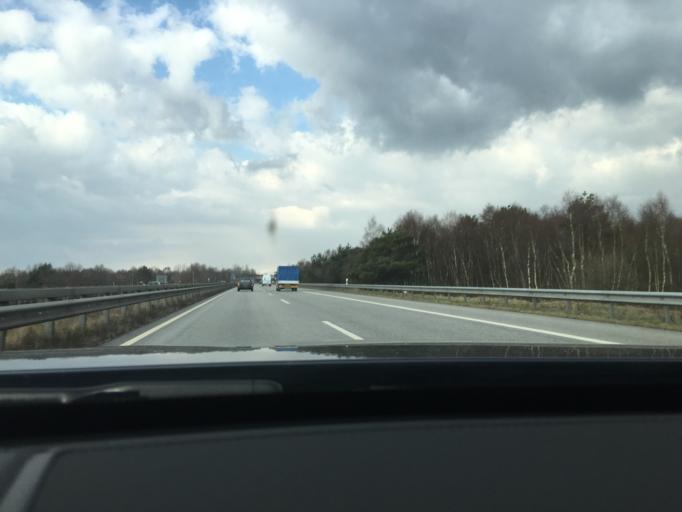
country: DE
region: Lower Saxony
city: Driftsethe
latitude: 53.3581
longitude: 8.5871
